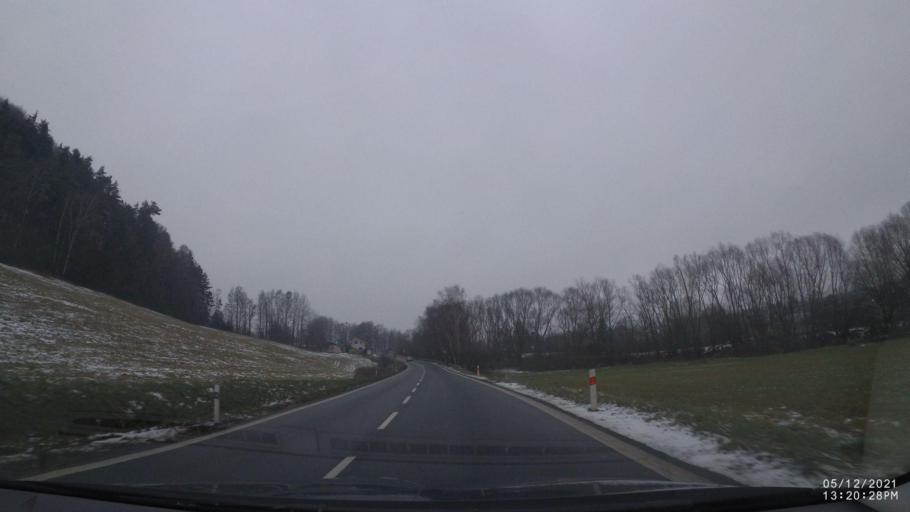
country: CZ
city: Velke Porici
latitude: 50.4504
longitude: 16.1886
